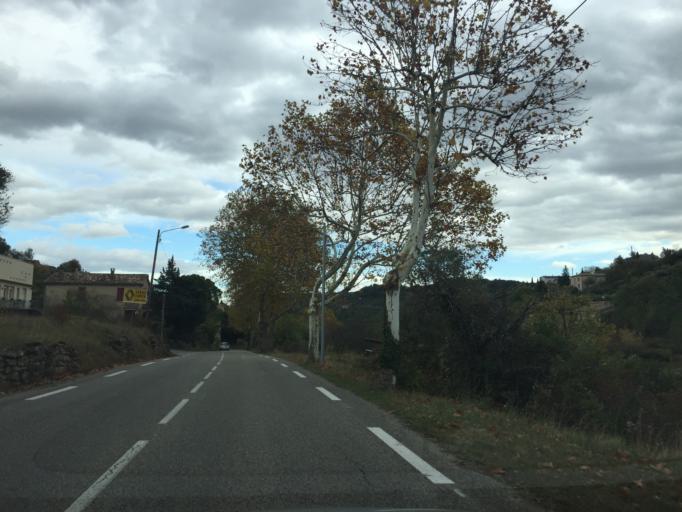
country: FR
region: Rhone-Alpes
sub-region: Departement de l'Ardeche
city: Les Vans
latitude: 44.4079
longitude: 4.1142
